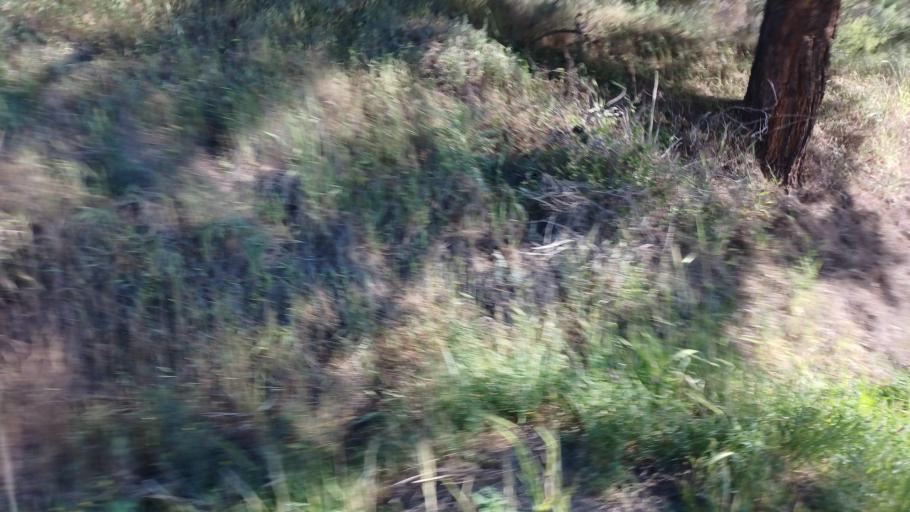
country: CY
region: Lefkosia
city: Peristerona
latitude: 35.0245
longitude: 33.0469
